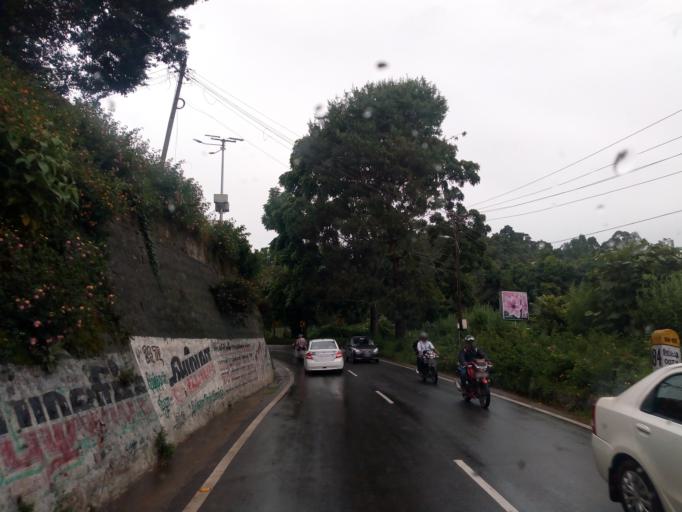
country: IN
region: Tamil Nadu
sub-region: Nilgiri
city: Wellington
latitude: 11.3588
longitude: 76.7840
